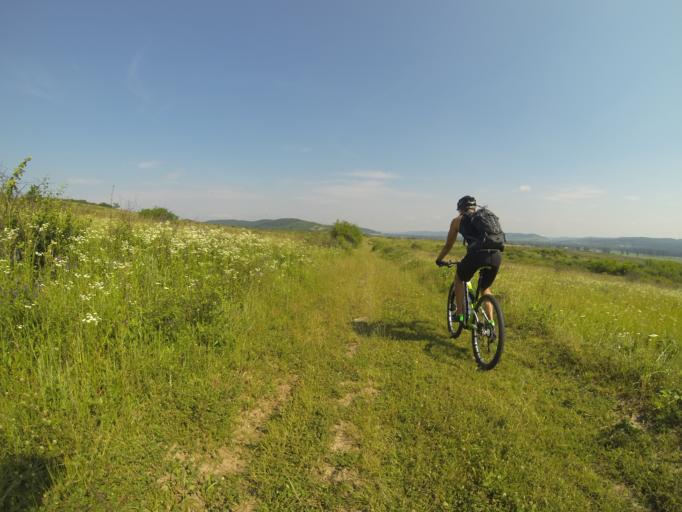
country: RO
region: Gorj
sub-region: Comuna Crusetu
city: Crusetu
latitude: 44.6100
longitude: 23.6692
